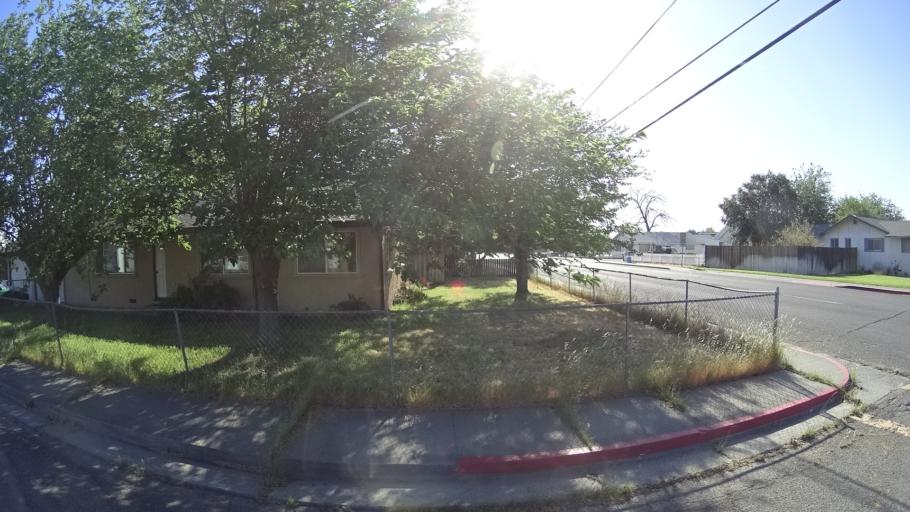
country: US
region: California
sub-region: Glenn County
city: Orland
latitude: 39.7402
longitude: -122.1860
